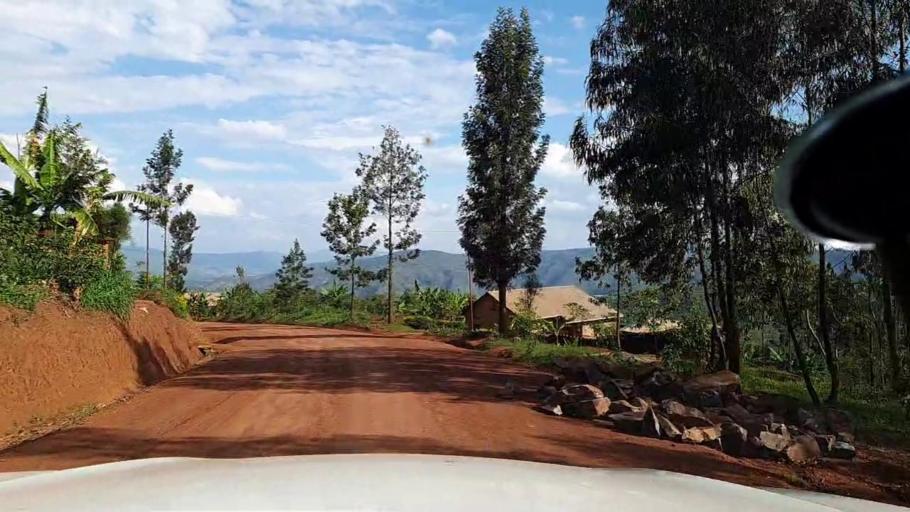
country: RW
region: Kigali
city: Kigali
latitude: -1.8379
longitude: 29.8495
